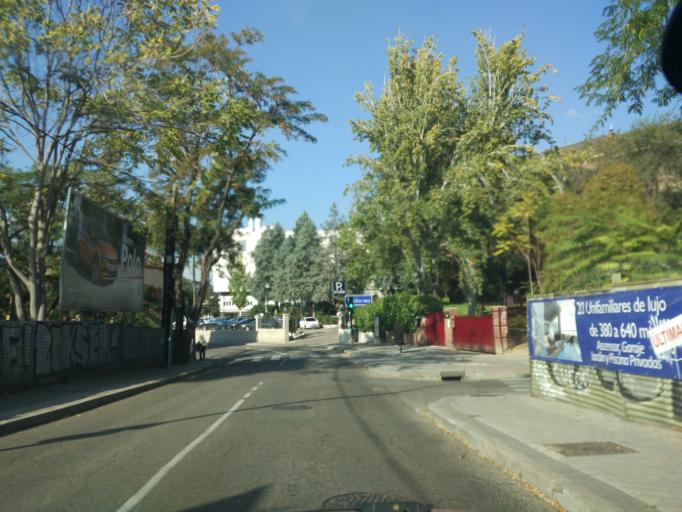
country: ES
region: Madrid
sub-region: Provincia de Madrid
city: Tetuan de las Victorias
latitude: 40.4674
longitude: -3.7244
